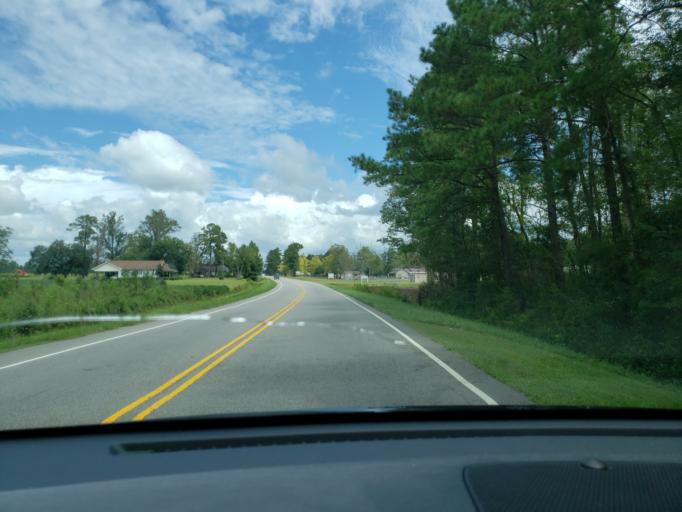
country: US
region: North Carolina
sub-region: Columbus County
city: Brunswick
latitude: 34.1953
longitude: -78.7681
